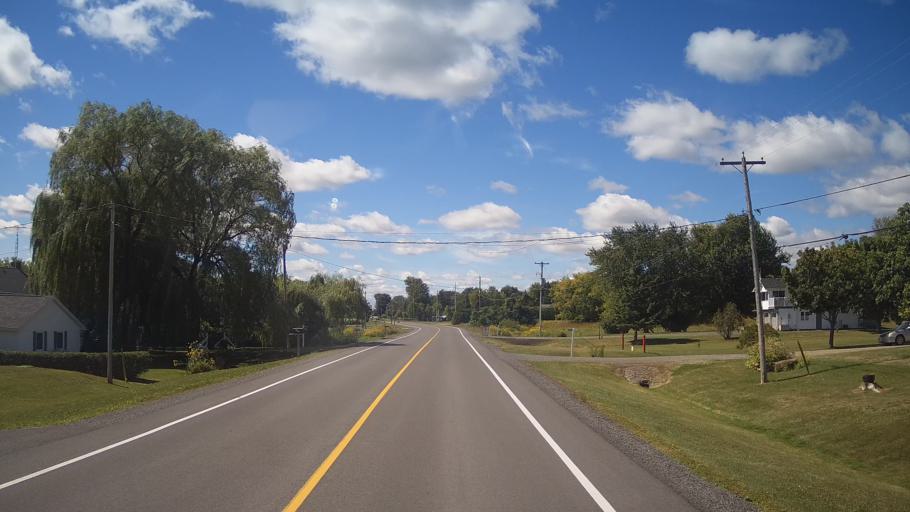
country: US
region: New York
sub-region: St. Lawrence County
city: Norfolk
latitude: 44.8672
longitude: -75.2499
